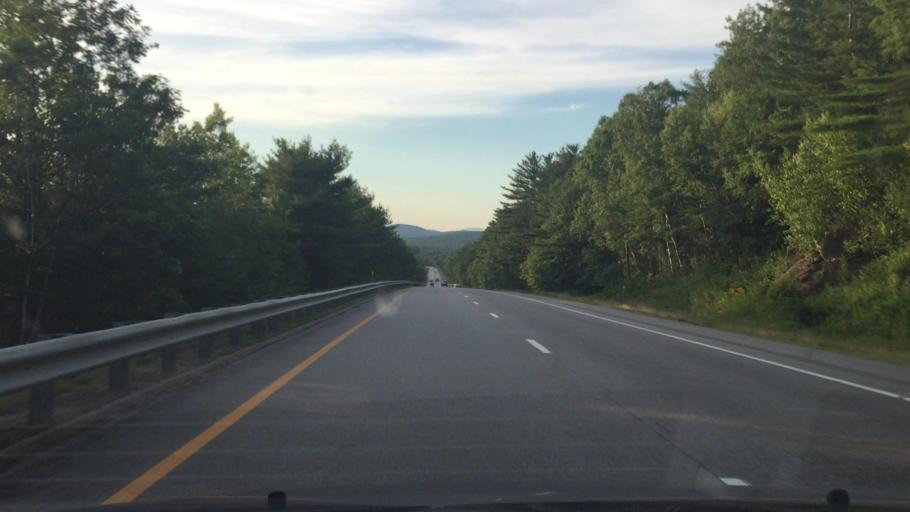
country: US
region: New Hampshire
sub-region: Grafton County
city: Ashland
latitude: 43.7256
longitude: -71.6561
